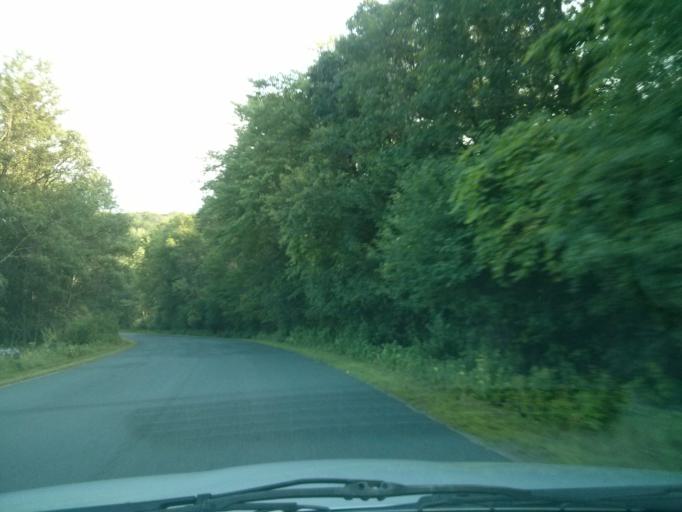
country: US
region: Wisconsin
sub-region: Saint Croix County
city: North Hudson
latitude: 45.0123
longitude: -92.7064
